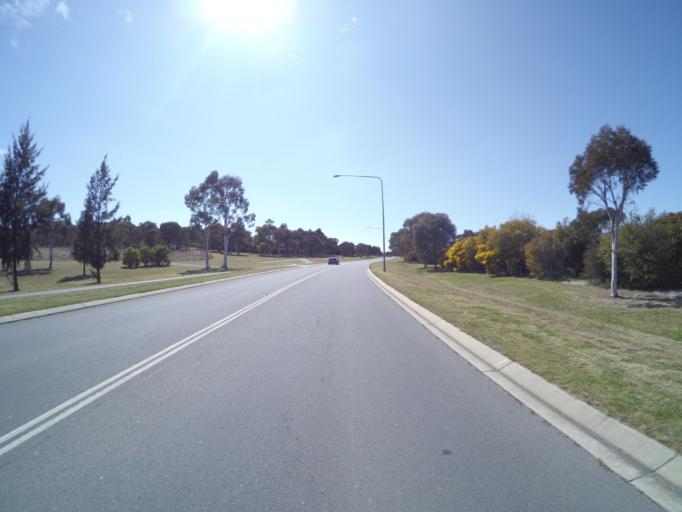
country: AU
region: Australian Capital Territory
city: Macarthur
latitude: -35.4446
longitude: 149.0807
